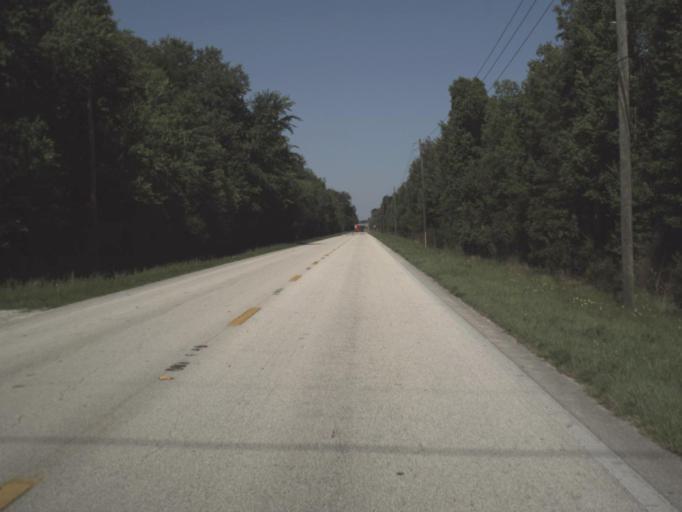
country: US
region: Florida
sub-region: Duval County
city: Baldwin
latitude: 30.3062
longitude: -81.9247
